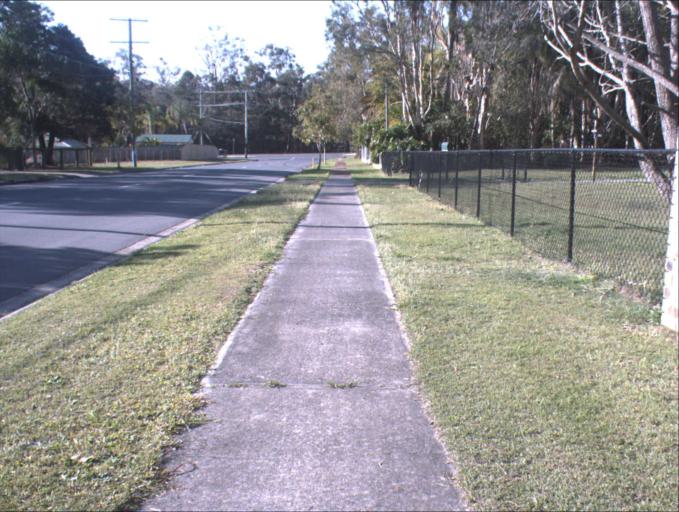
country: AU
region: Queensland
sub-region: Logan
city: Park Ridge South
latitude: -27.7004
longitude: 153.0268
